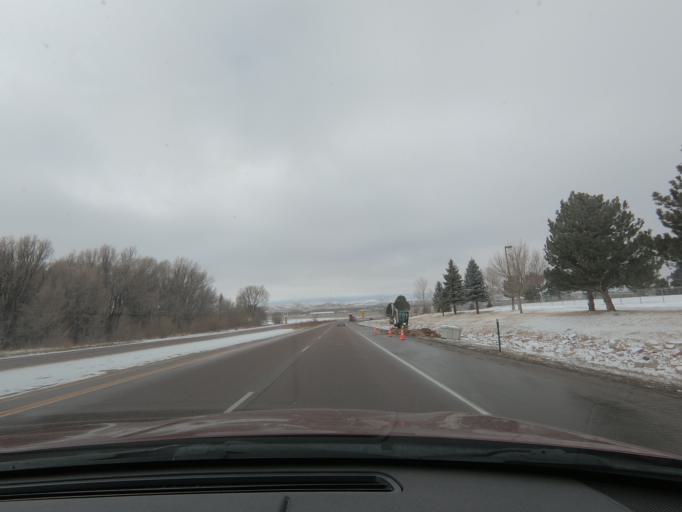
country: US
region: Colorado
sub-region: El Paso County
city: Security-Widefield
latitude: 38.7201
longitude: -104.7066
